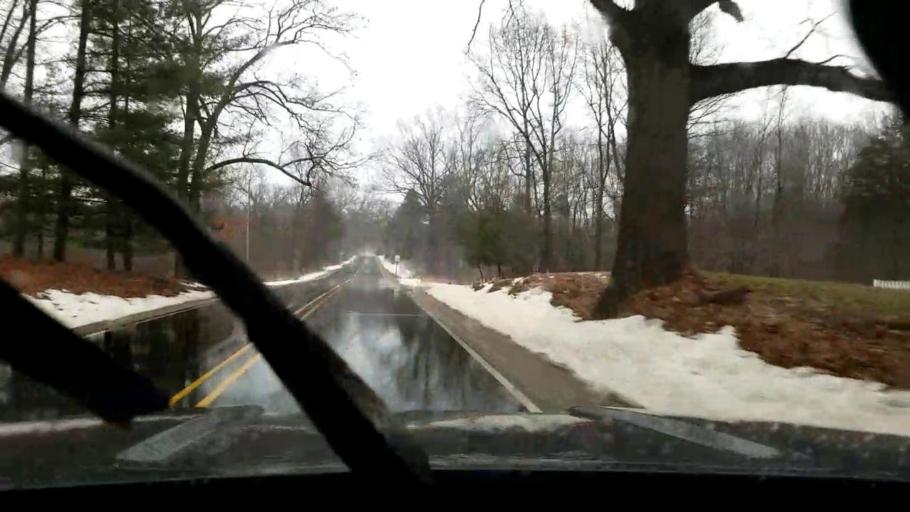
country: US
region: Michigan
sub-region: Jackson County
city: Michigan Center
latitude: 42.3142
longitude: -84.3089
